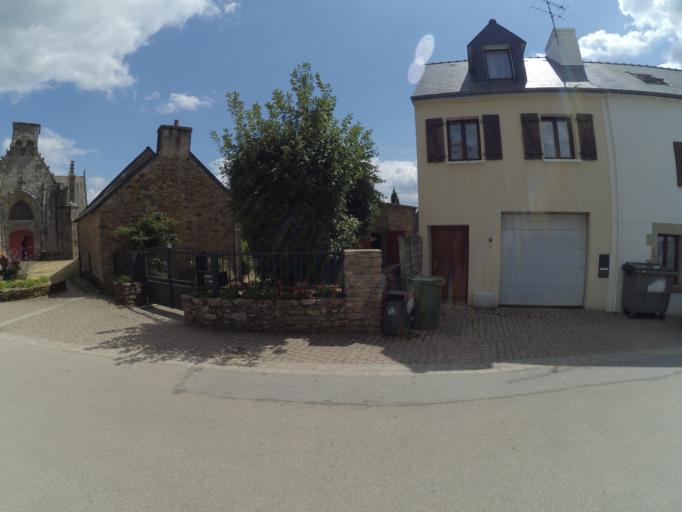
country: FR
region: Brittany
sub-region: Departement du Morbihan
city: Landaul
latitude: 47.7481
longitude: -3.0758
